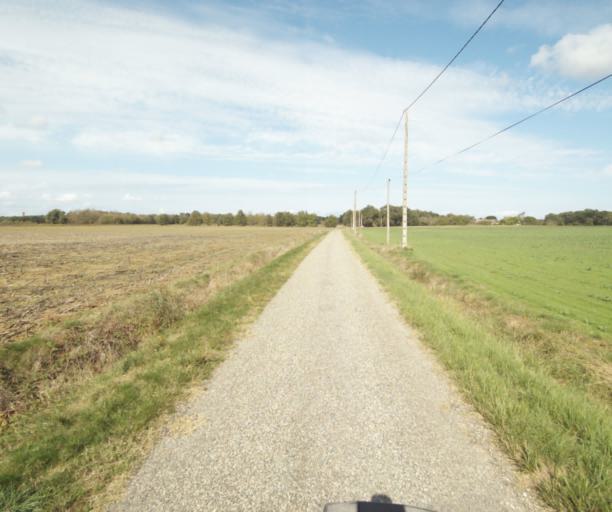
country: FR
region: Midi-Pyrenees
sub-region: Departement du Tarn-et-Garonne
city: Verdun-sur-Garonne
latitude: 43.8472
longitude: 1.1778
